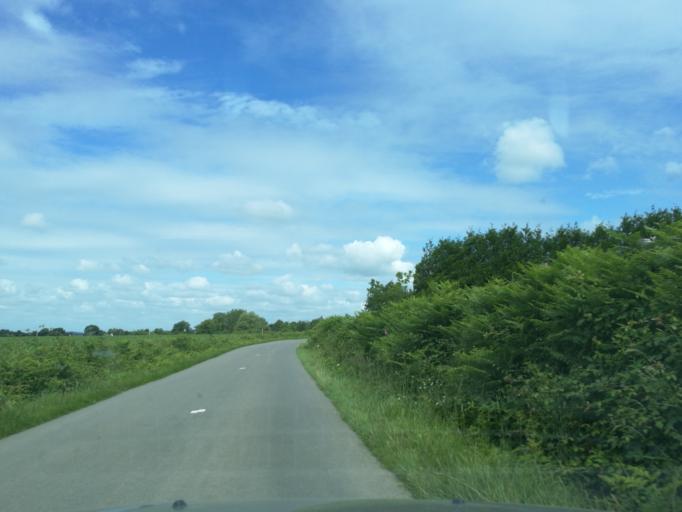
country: FR
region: Brittany
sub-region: Departement d'Ille-et-Vilaine
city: Montfort-sur-Meu
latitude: 48.1592
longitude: -1.9709
